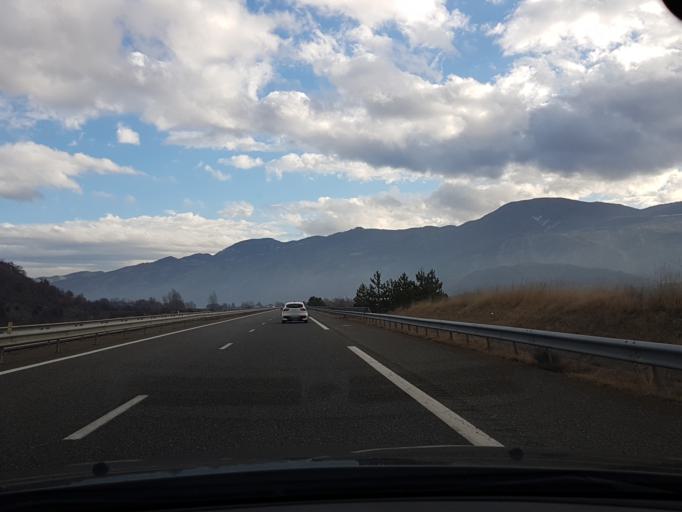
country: FR
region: Provence-Alpes-Cote d'Azur
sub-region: Departement des Hautes-Alpes
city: Tallard
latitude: 44.4183
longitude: 5.9822
